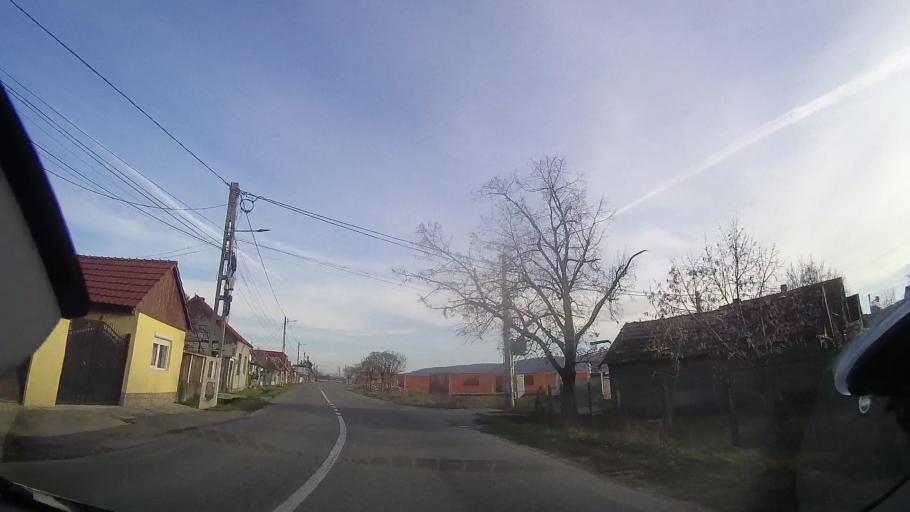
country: RO
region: Bihor
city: Lugasu de Jos
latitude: 47.0449
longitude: 22.3322
